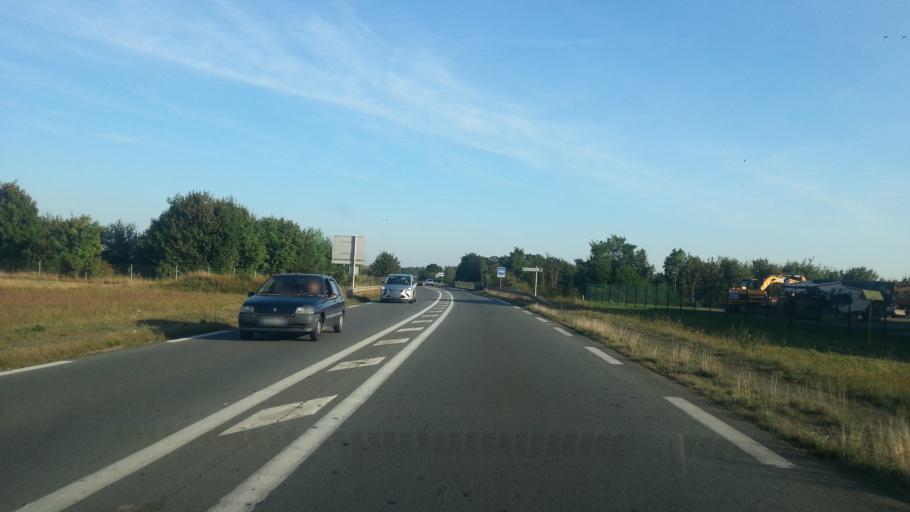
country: FR
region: Picardie
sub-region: Departement de l'Oise
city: Allonne
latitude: 49.4285
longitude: 2.1275
